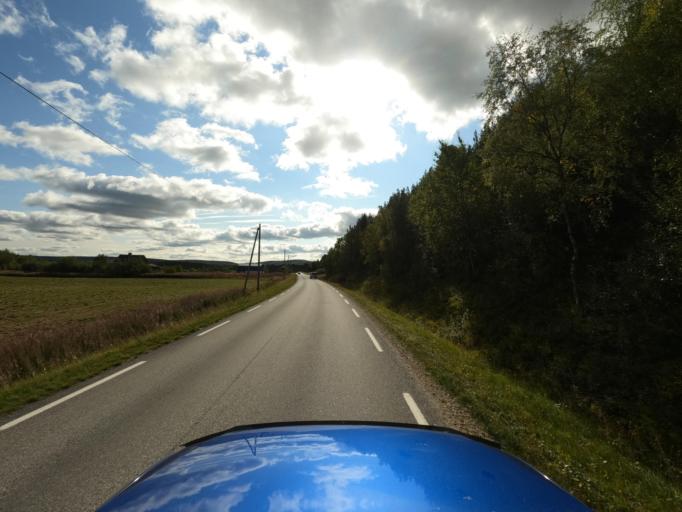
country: NO
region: Finnmark Fylke
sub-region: Karasjok
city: Karasjohka
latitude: 69.4081
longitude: 25.8064
